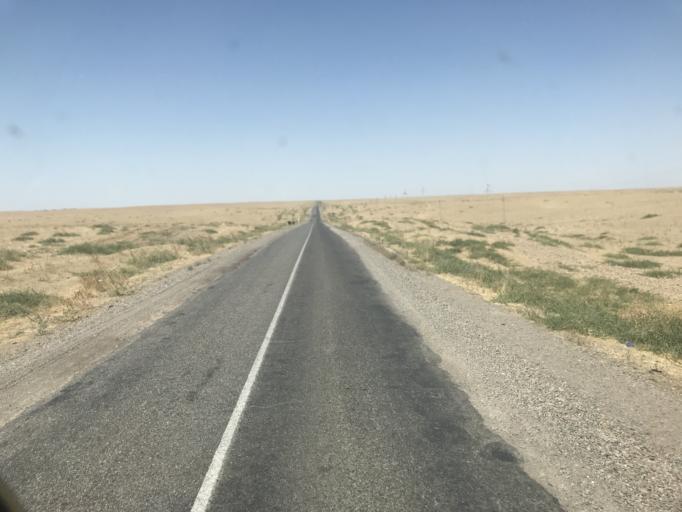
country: UZ
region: Toshkent
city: Chinoz
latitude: 41.1434
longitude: 68.6972
